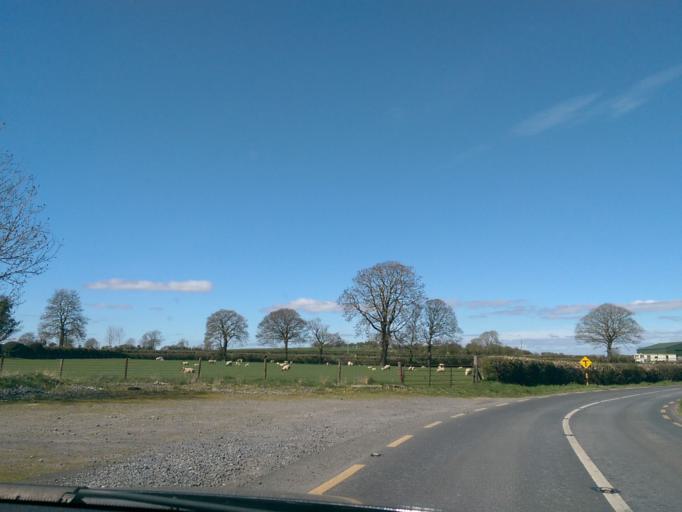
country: IE
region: Leinster
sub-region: Kildare
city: Moone
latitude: 52.9774
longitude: -6.7754
